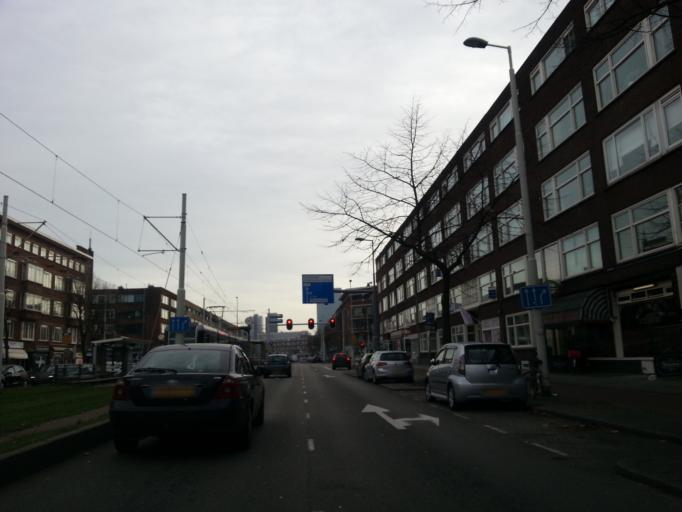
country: NL
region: South Holland
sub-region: Gemeente Rotterdam
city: Rotterdam
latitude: 51.9346
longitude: 4.4645
